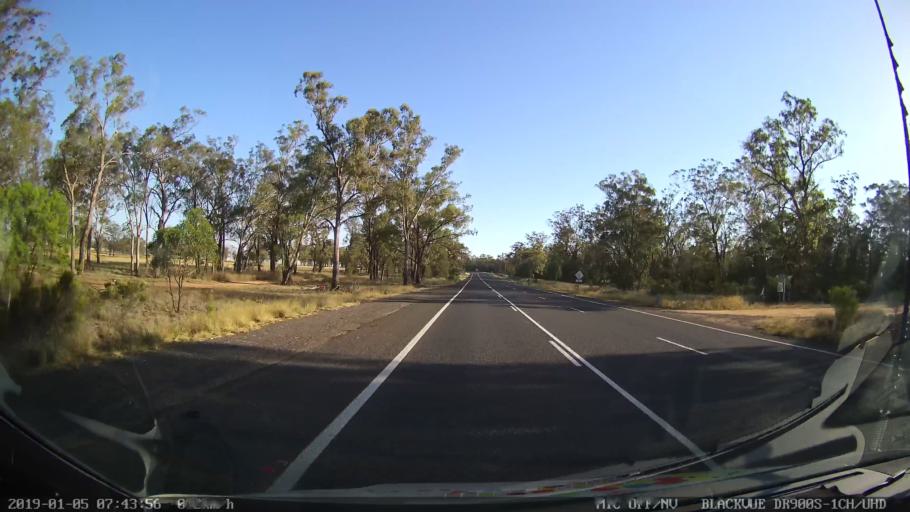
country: AU
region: New South Wales
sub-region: Gilgandra
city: Gilgandra
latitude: -31.8789
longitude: 148.6371
